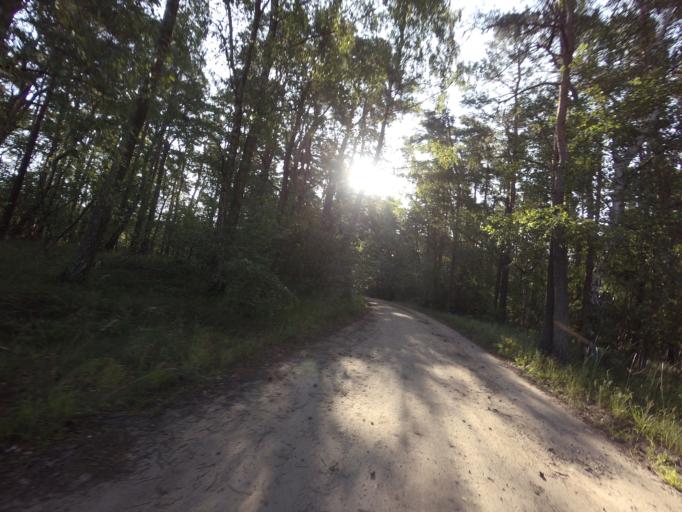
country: SE
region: Skane
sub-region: Landskrona
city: Asmundtorp
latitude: 55.8436
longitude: 12.9264
